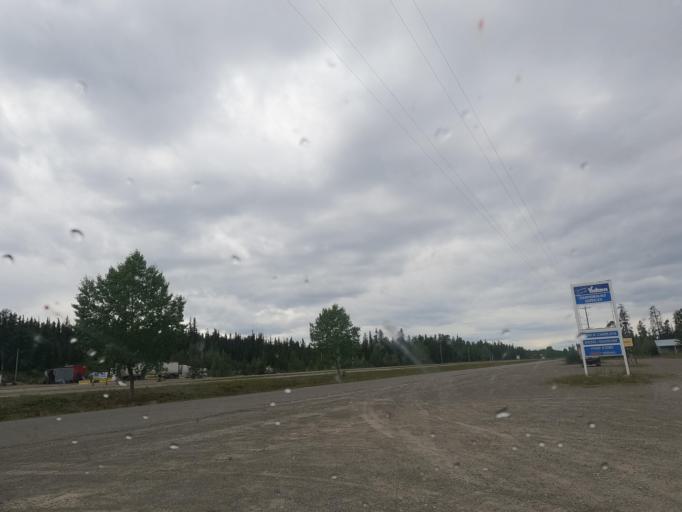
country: CA
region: Yukon
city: Watson Lake
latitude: 60.0502
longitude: -128.6549
